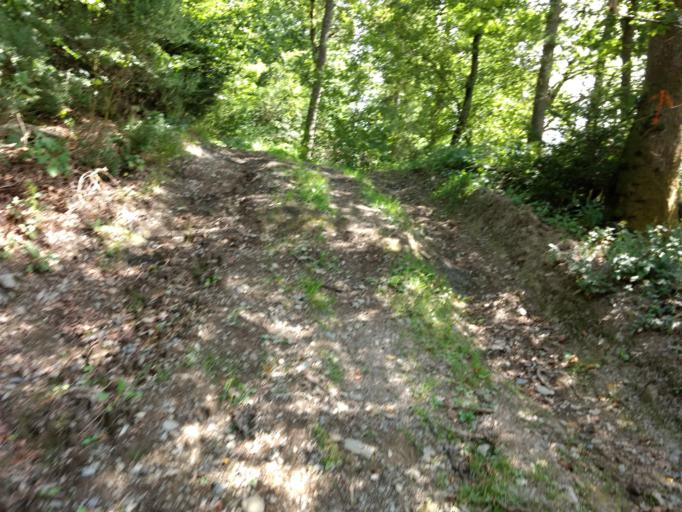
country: BE
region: Wallonia
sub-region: Province du Luxembourg
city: Houffalize
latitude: 50.1433
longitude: 5.7323
